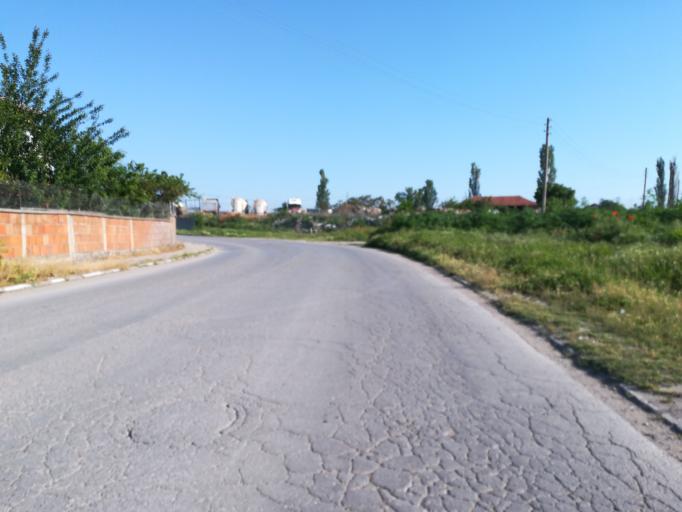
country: BG
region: Stara Zagora
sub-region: Obshtina Chirpan
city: Chirpan
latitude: 42.1070
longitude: 25.2272
